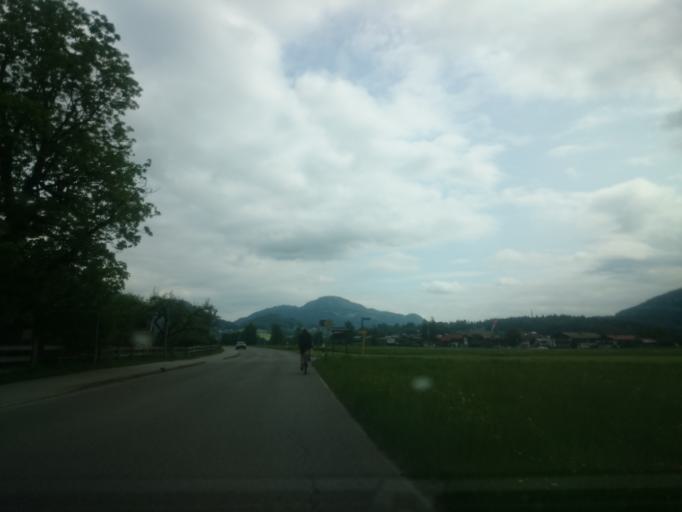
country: DE
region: Bavaria
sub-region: Upper Bavaria
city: Schoenau am Koenigssee
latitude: 47.6082
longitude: 12.9741
